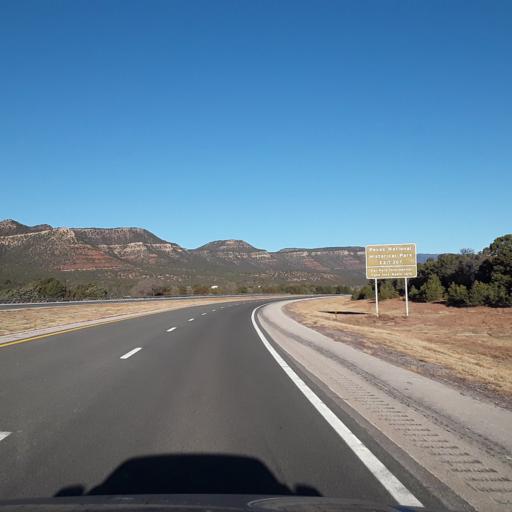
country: US
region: New Mexico
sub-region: San Miguel County
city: Pecos
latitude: 35.4809
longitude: -105.6677
